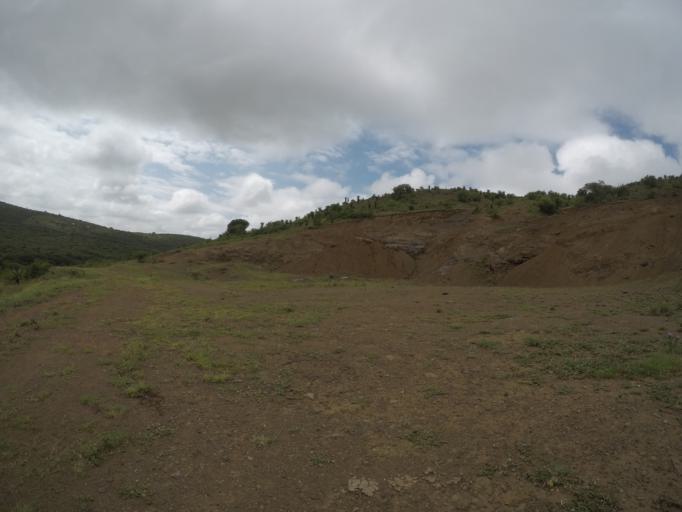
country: ZA
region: KwaZulu-Natal
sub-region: uThungulu District Municipality
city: Empangeni
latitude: -28.6272
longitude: 31.8782
